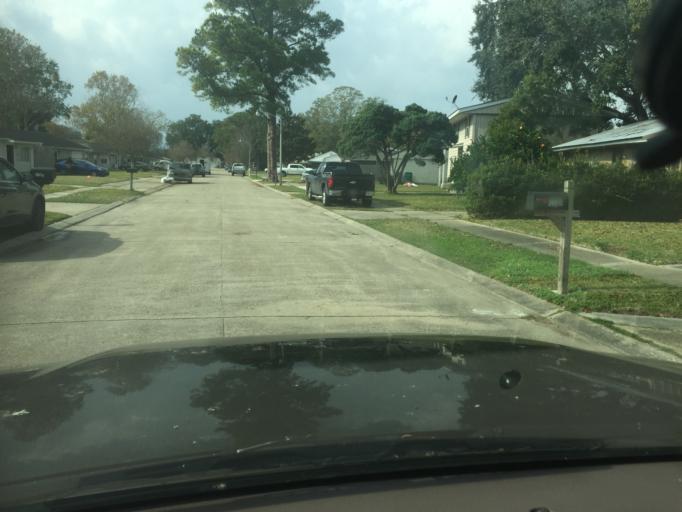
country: US
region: Louisiana
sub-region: Jefferson Parish
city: Avondale
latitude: 29.9139
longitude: -90.2032
